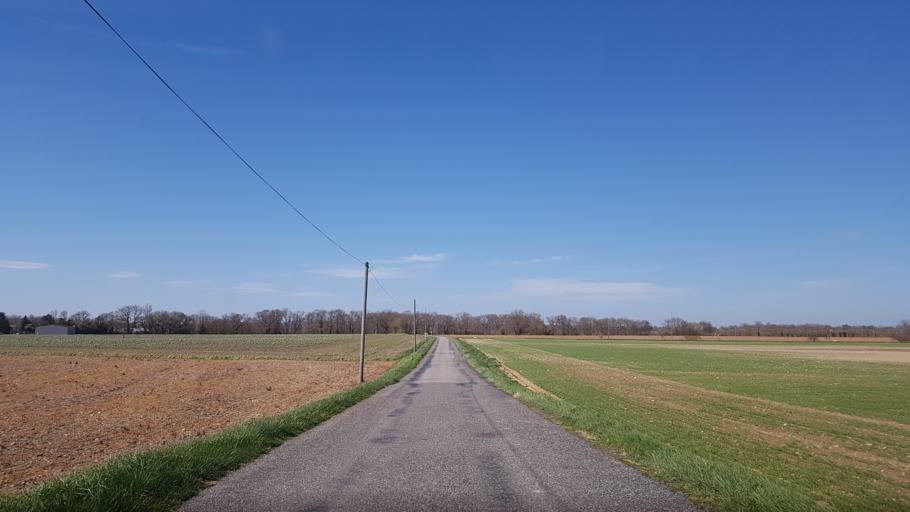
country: FR
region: Languedoc-Roussillon
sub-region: Departement de l'Aude
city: Belpech
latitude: 43.1807
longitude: 1.7116
